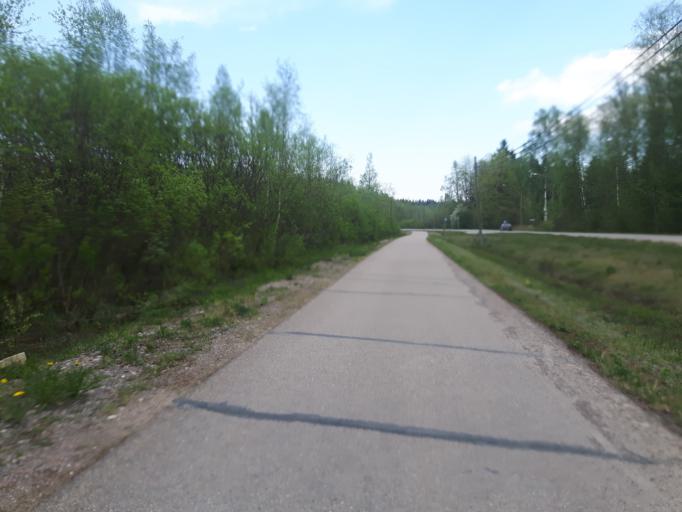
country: FI
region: Uusimaa
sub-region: Porvoo
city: Porvoo
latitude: 60.4024
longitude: 25.7152
